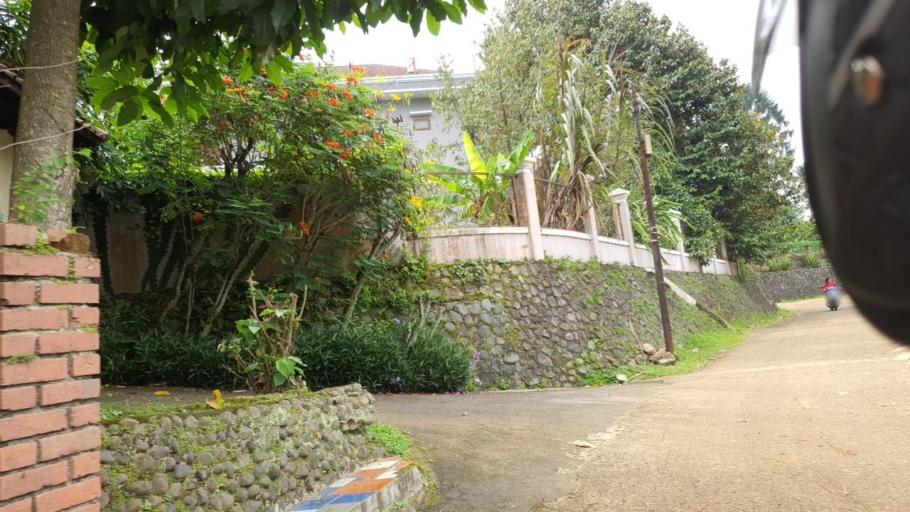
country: ID
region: West Java
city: Caringin
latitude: -6.6540
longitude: 106.8844
